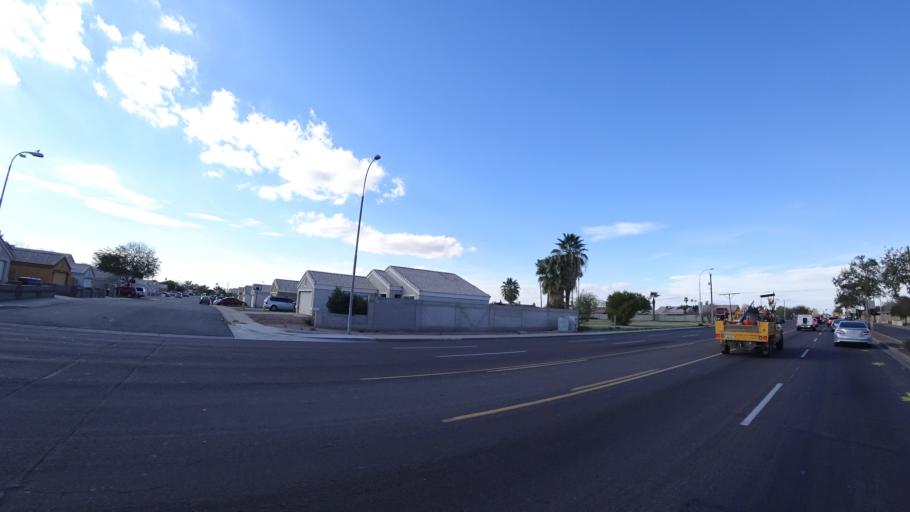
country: US
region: Arizona
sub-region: Maricopa County
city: Tolleson
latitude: 33.4845
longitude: -112.2377
